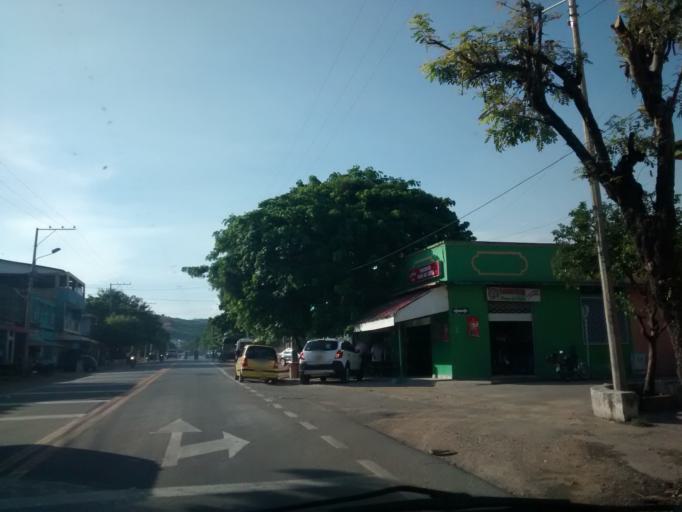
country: CO
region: Cundinamarca
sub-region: Girardot
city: Girardot City
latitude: 4.3075
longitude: -74.8038
